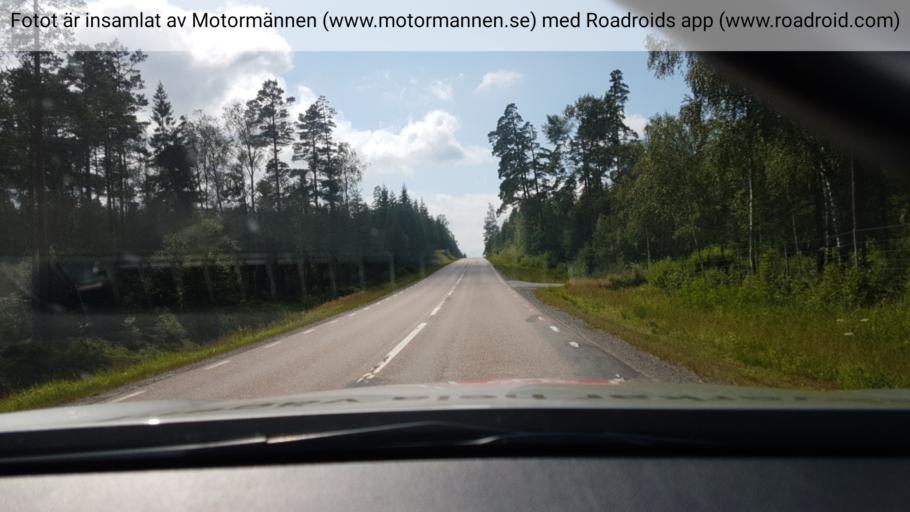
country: SE
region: Vaestra Goetaland
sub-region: Marks Kommun
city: Fritsla
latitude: 57.4917
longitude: 12.8454
